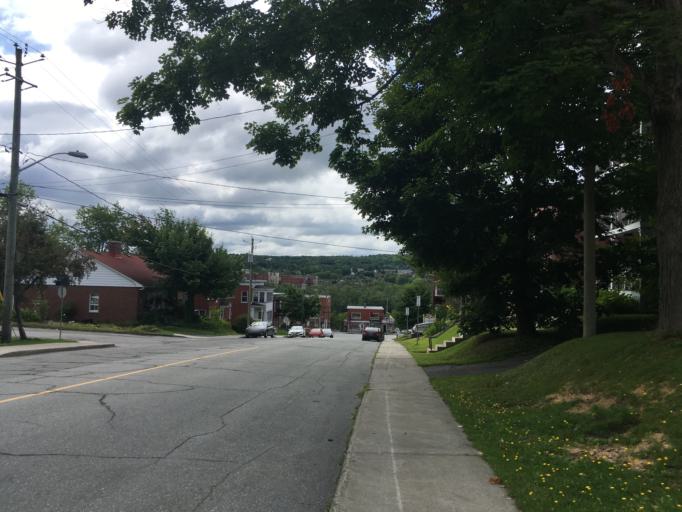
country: CA
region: Quebec
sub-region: Estrie
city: Sherbrooke
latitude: 45.4000
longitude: -71.9080
